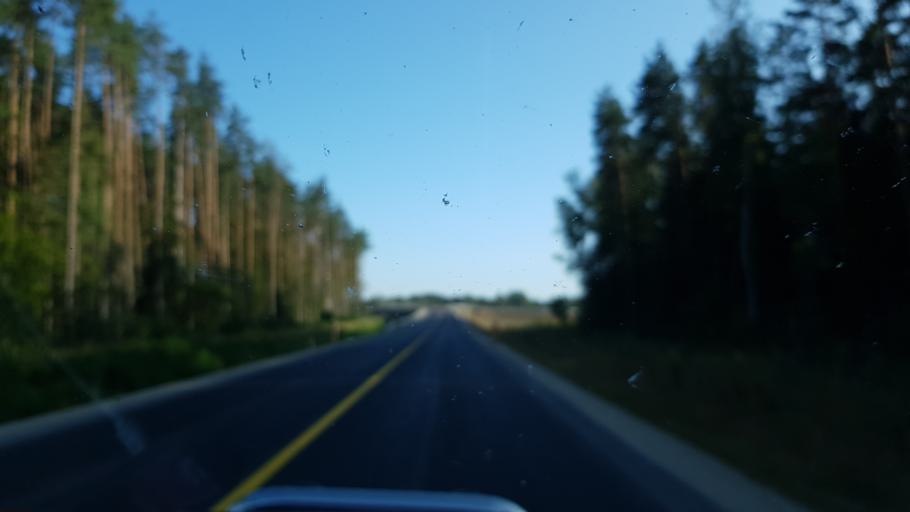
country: EE
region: Harju
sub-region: Raasiku vald
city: Raasiku
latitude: 59.1624
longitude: 25.1902
